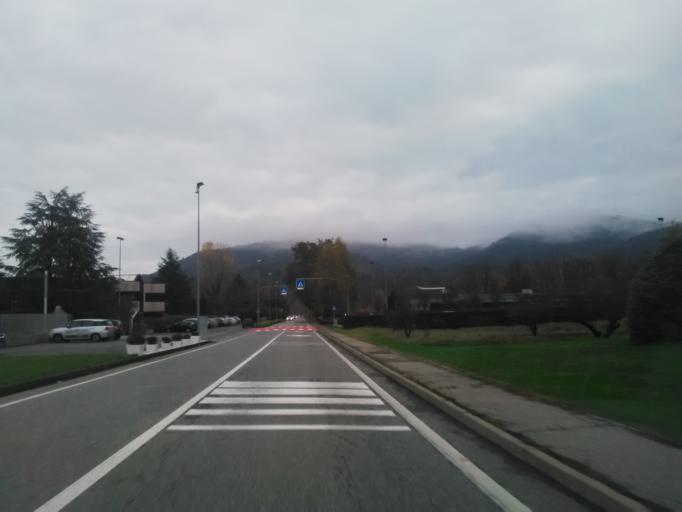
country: IT
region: Piedmont
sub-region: Provincia di Novara
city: Grignasco
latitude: 45.6598
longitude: 8.3346
